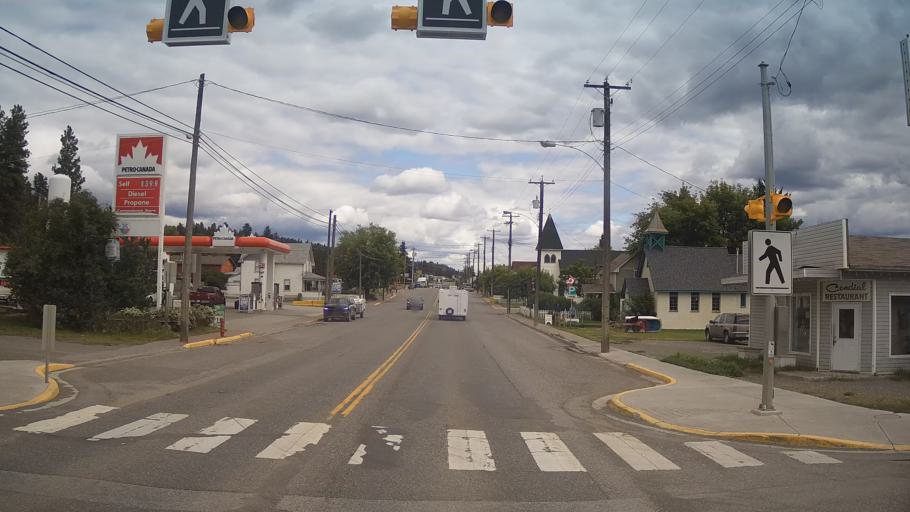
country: CA
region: British Columbia
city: Cache Creek
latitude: 51.0898
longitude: -121.5893
